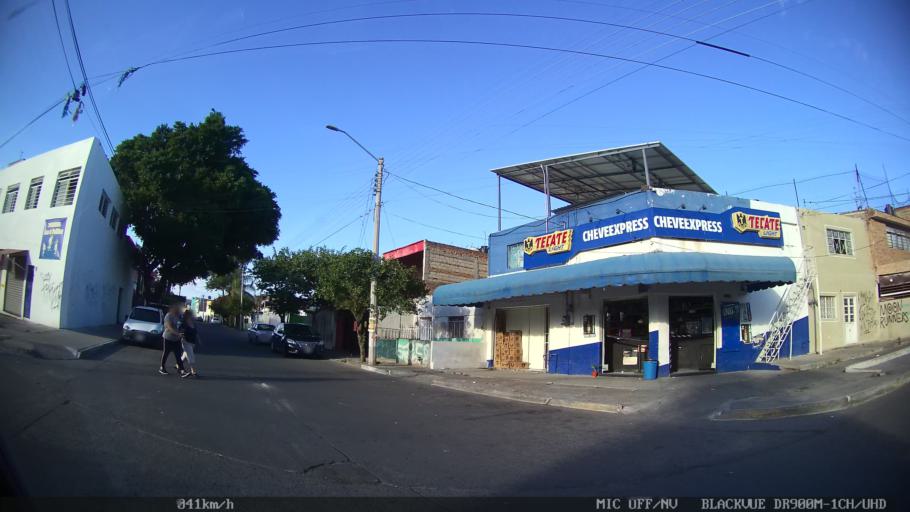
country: MX
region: Jalisco
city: Tlaquepaque
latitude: 20.7032
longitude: -103.3121
